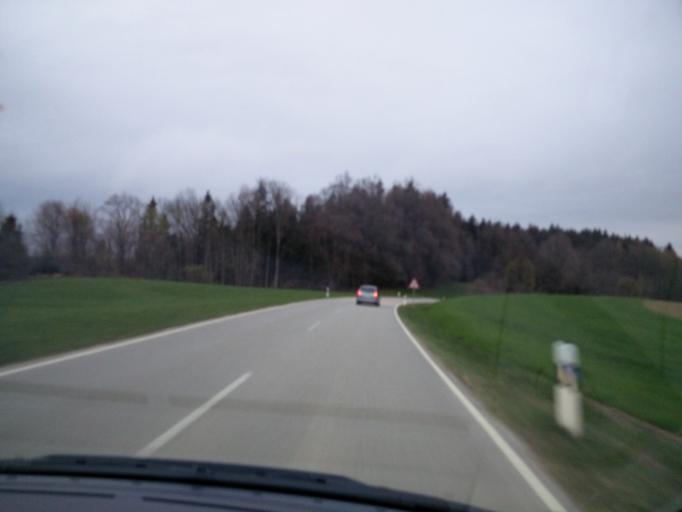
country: DE
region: Bavaria
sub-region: Upper Bavaria
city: Amerang
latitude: 47.9827
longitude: 12.2992
